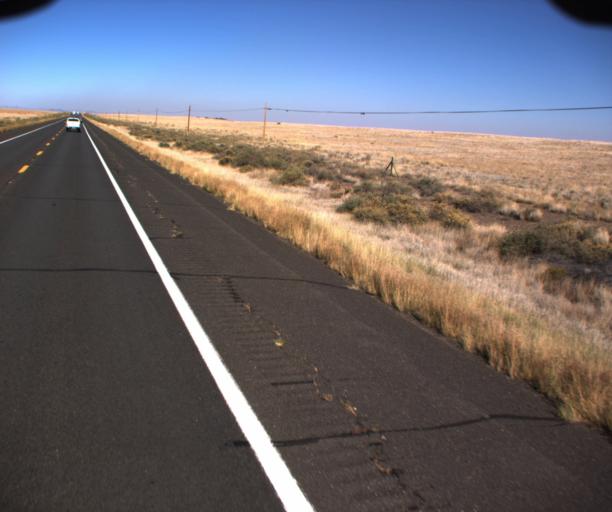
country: US
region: Arizona
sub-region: Coconino County
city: Flagstaff
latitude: 35.6123
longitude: -111.5236
